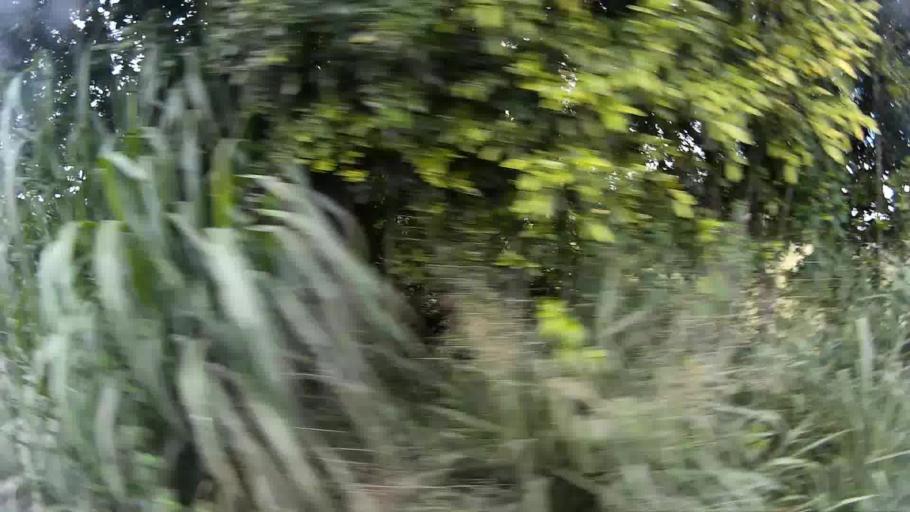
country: CO
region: Valle del Cauca
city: Ulloa
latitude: 4.7524
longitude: -75.7136
